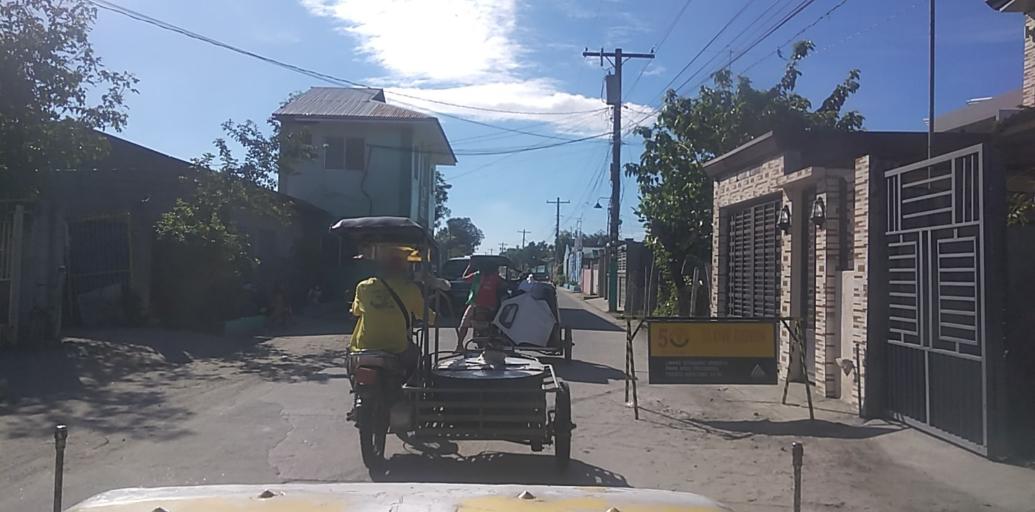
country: PH
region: Central Luzon
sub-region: Province of Pampanga
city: San Patricio
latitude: 15.1100
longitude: 120.7120
